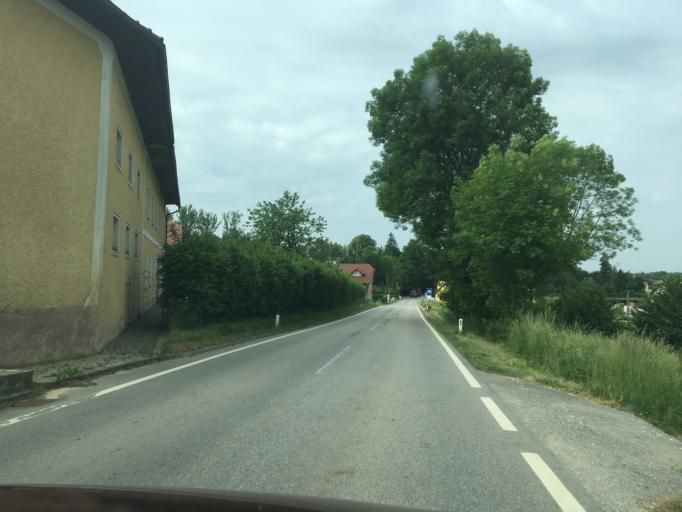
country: AT
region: Upper Austria
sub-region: Politischer Bezirk Grieskirchen
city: Grieskirchen
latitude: 48.3362
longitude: 13.8633
